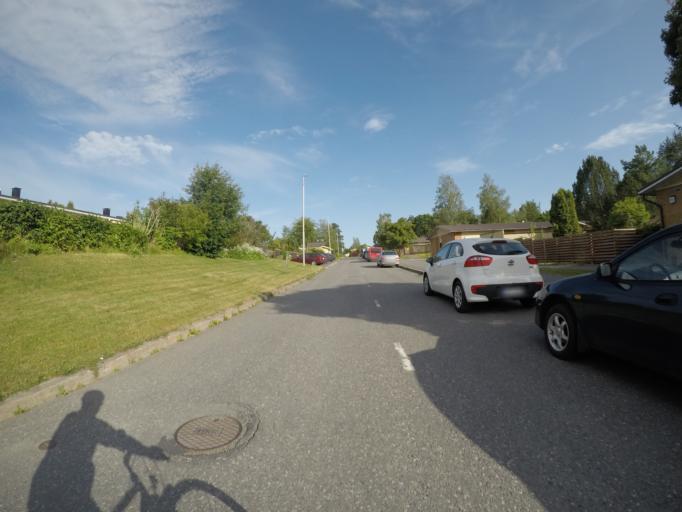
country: FI
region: Haeme
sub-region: Haemeenlinna
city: Haemeenlinna
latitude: 60.9782
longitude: 24.3993
